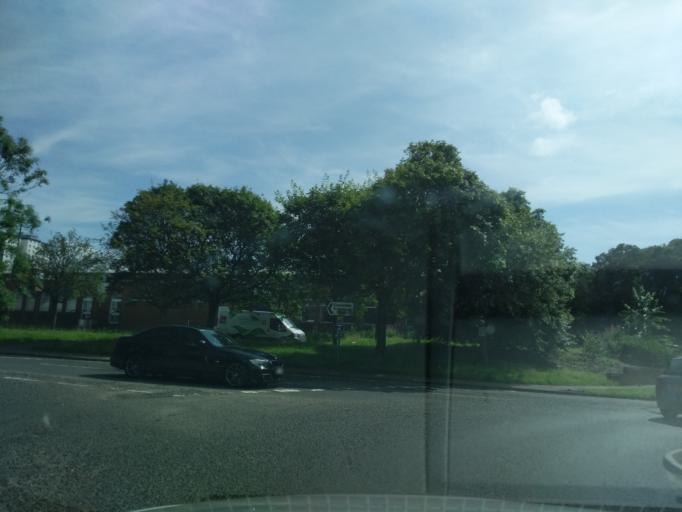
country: GB
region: Scotland
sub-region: Dundee City
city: Dundee
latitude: 56.4804
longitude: -3.0185
